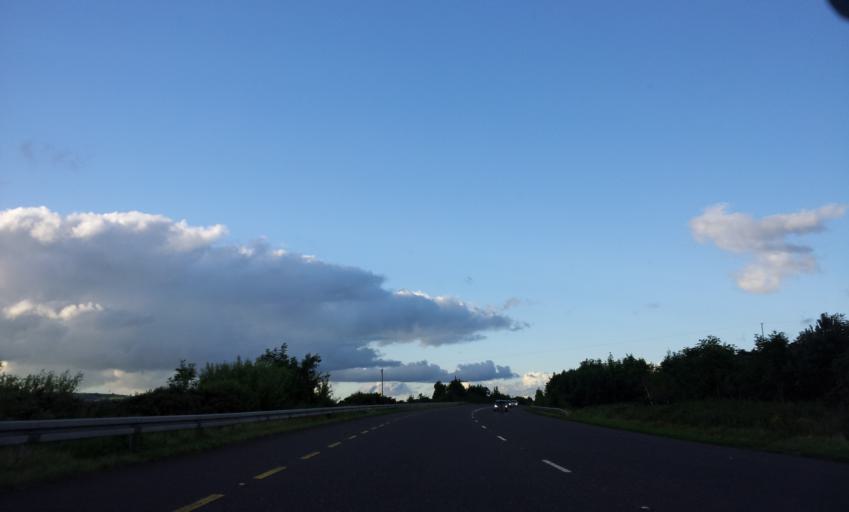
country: IE
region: Munster
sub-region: County Limerick
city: Abbeyfeale
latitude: 52.3282
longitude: -9.3592
